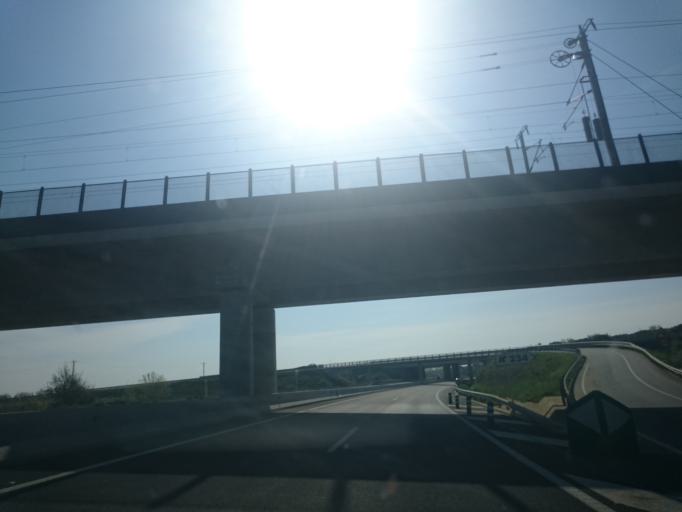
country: ES
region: Catalonia
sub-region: Provincia de Girona
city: Vilobi d'Onyar
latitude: 41.8742
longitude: 2.7593
